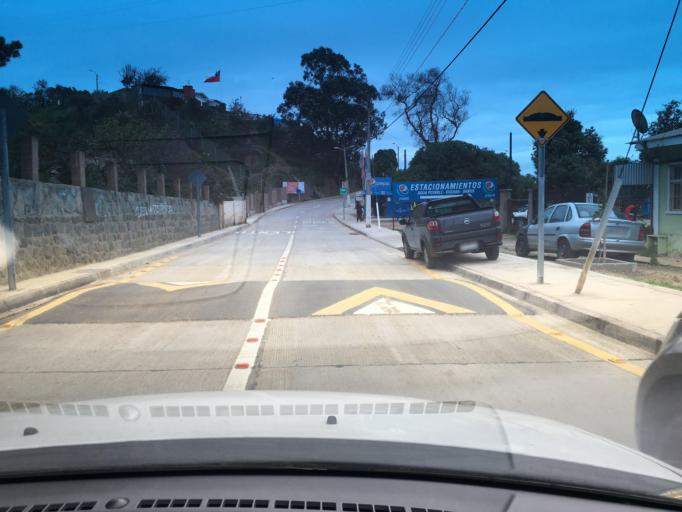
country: CL
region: Valparaiso
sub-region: Provincia de Valparaiso
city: Valparaiso
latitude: -33.1026
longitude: -71.6705
